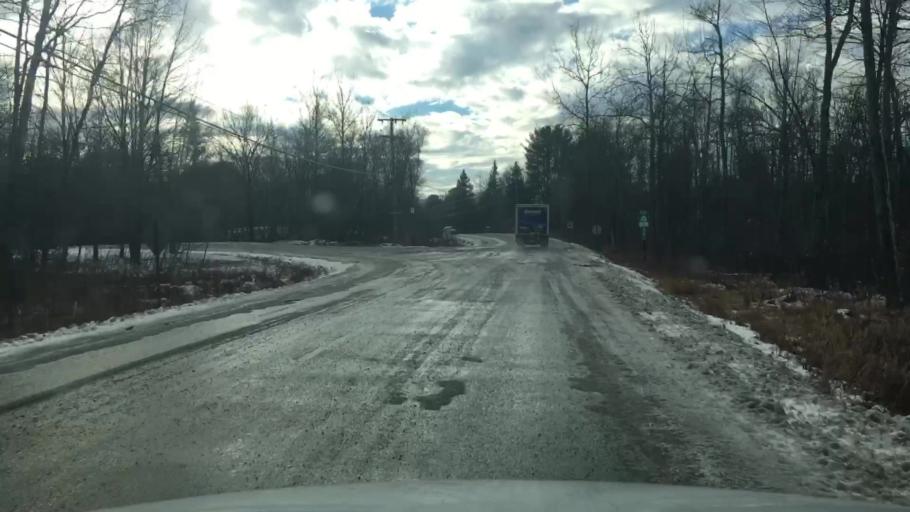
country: US
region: Maine
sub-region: Penobscot County
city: Brewer
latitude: 44.7284
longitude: -68.7556
